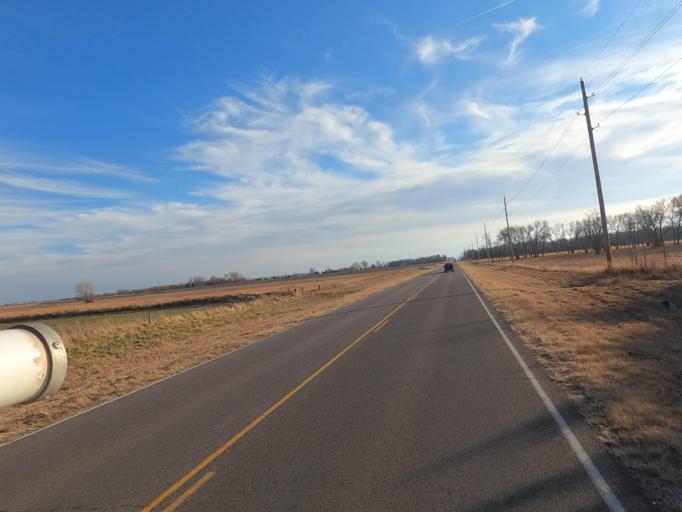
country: US
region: Kansas
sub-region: Reno County
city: Buhler
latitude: 38.0414
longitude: -97.7753
